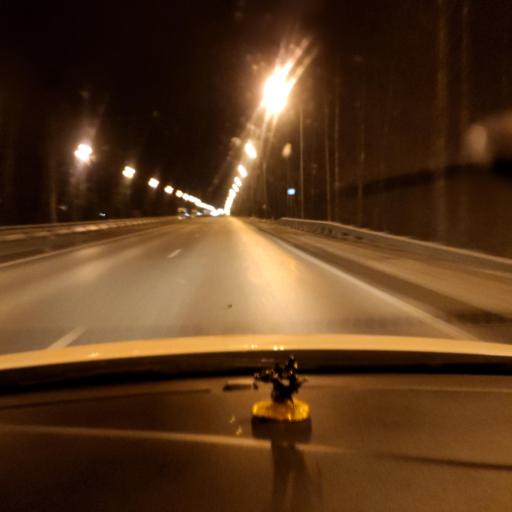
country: RU
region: Tatarstan
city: Osinovo
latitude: 55.8419
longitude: 48.8518
